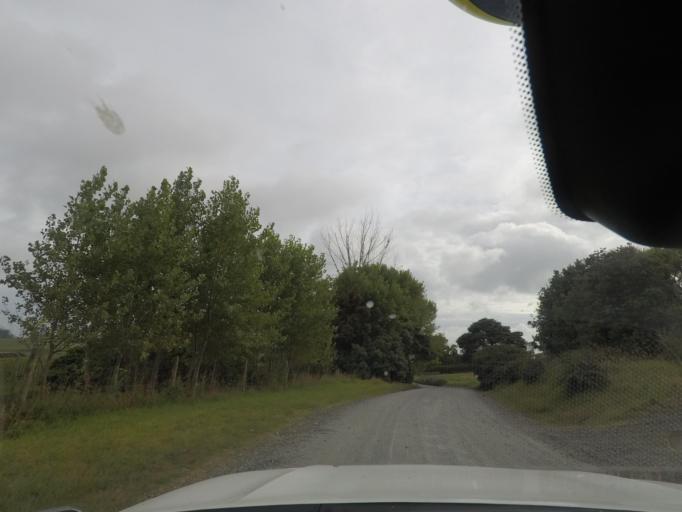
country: NZ
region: Auckland
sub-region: Auckland
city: Parakai
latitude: -36.4767
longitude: 174.2567
